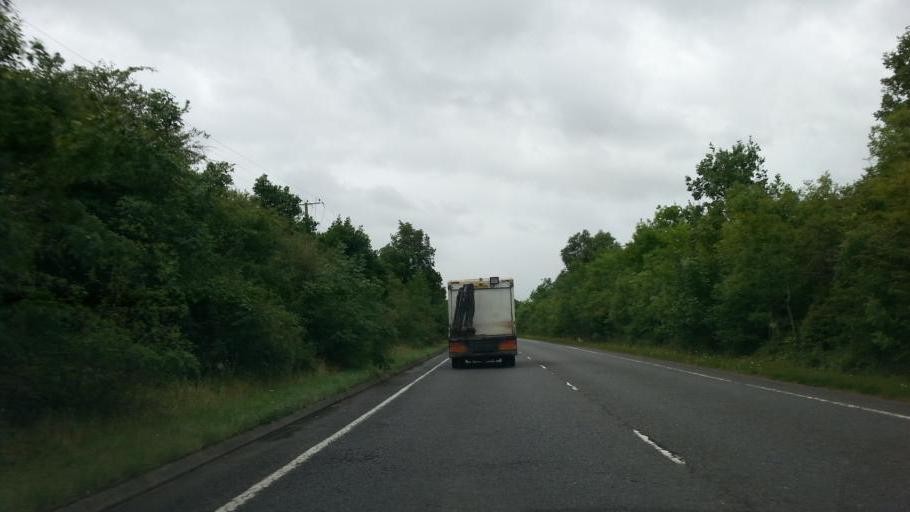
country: GB
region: England
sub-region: Northamptonshire
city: Oundle
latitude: 52.4599
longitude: -0.4623
